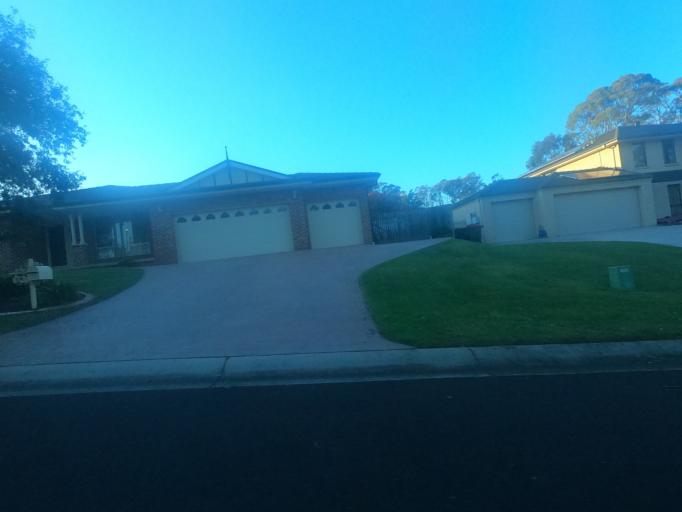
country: AU
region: New South Wales
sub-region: Wollongong
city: Dapto
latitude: -34.4915
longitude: 150.7654
